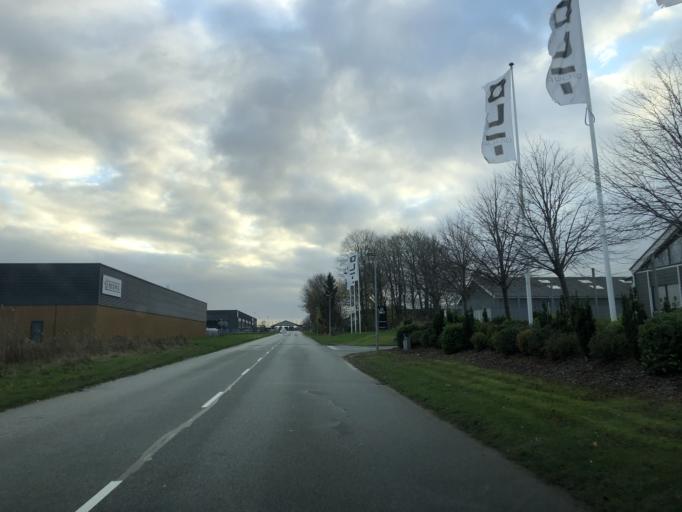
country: DK
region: Central Jutland
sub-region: Viborg Kommune
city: Viborg
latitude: 56.4628
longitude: 9.3687
